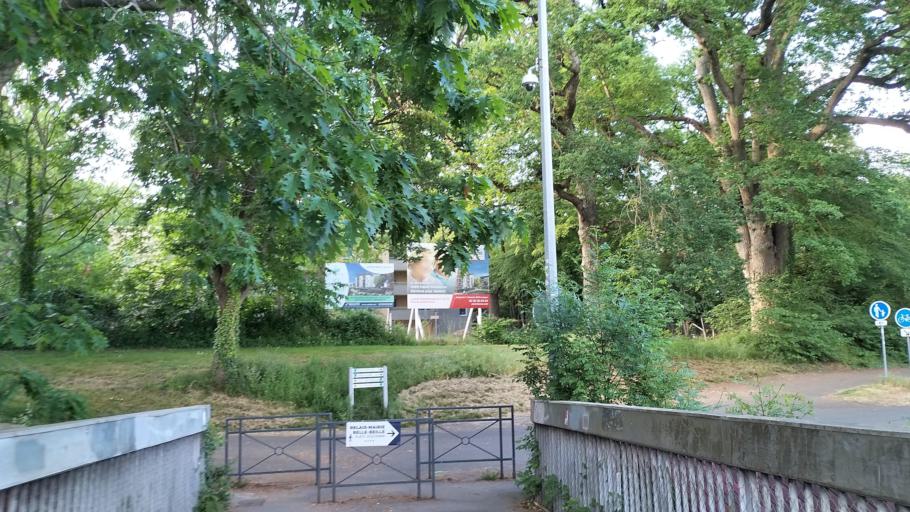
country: FR
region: Pays de la Loire
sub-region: Departement de Maine-et-Loire
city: Beaucouze
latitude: 47.4696
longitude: -0.5976
